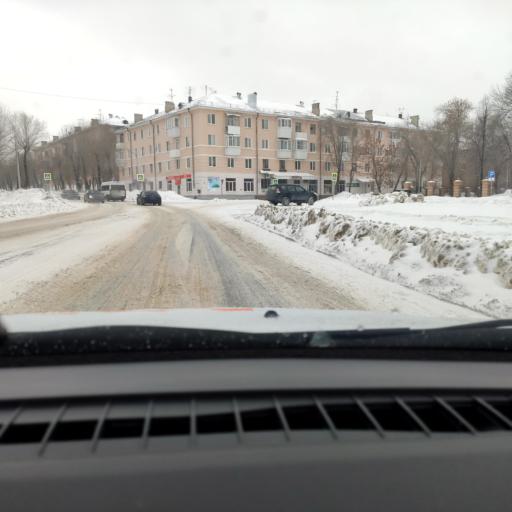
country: RU
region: Samara
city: Novokuybyshevsk
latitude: 53.0979
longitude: 49.9462
